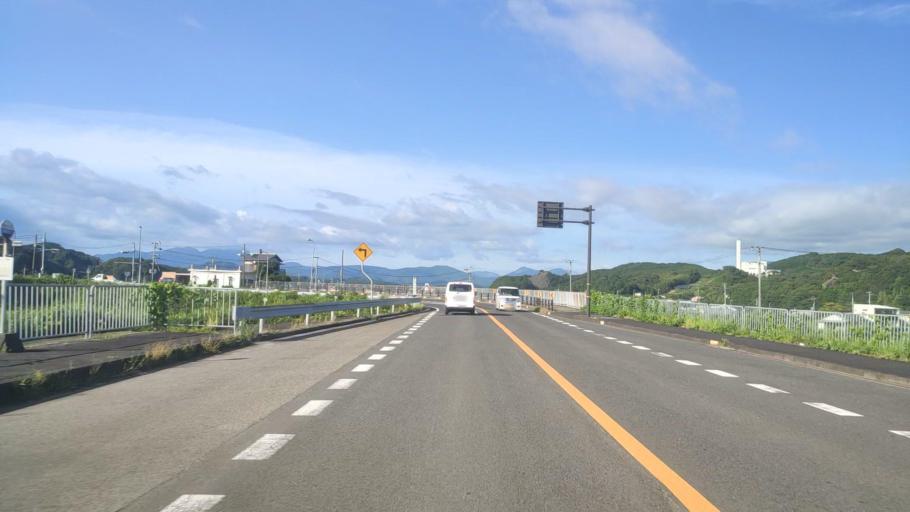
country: JP
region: Wakayama
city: Tanabe
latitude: 33.6786
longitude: 135.4093
